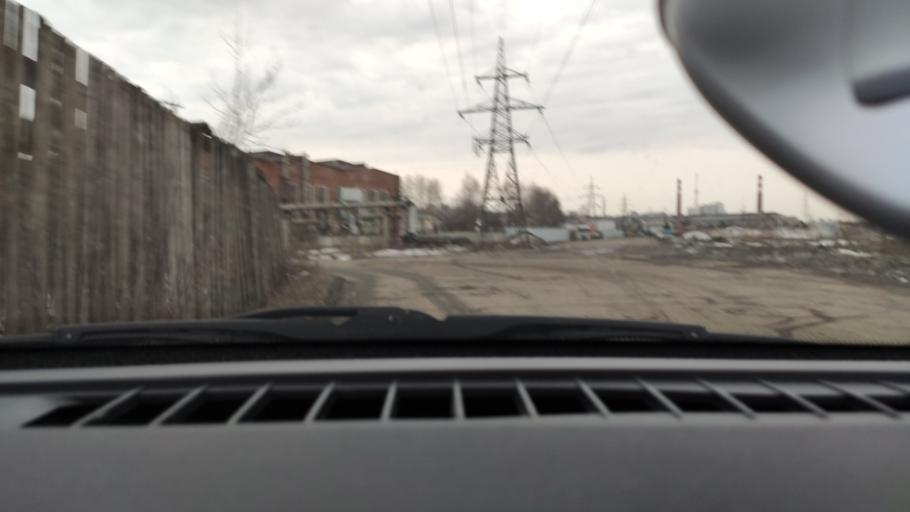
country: RU
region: Perm
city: Perm
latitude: 58.0409
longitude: 56.3062
